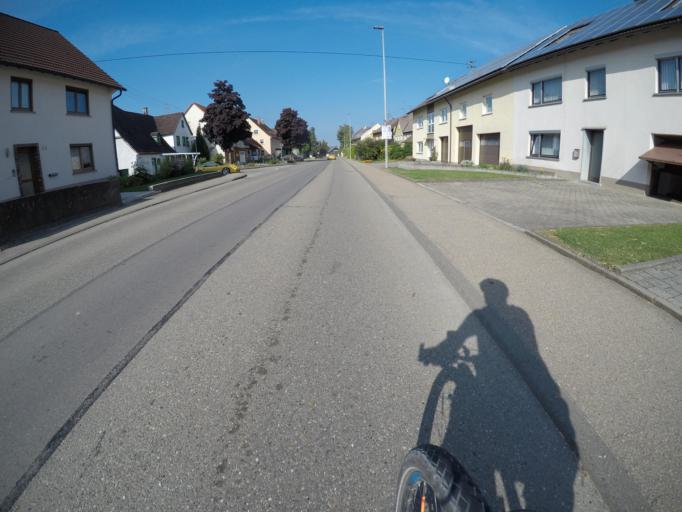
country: DE
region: Baden-Wuerttemberg
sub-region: Regierungsbezirk Stuttgart
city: Bohmenkirch
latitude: 48.6405
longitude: 9.9624
